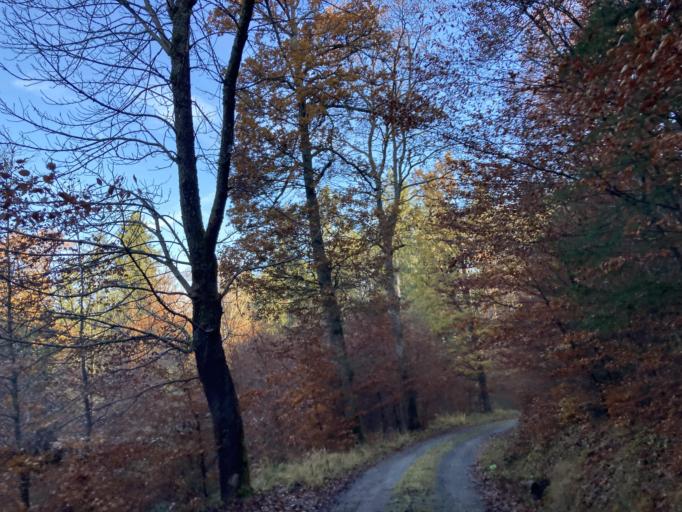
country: DE
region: Baden-Wuerttemberg
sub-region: Regierungsbezirk Stuttgart
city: Altdorf
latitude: 48.5829
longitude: 8.9987
